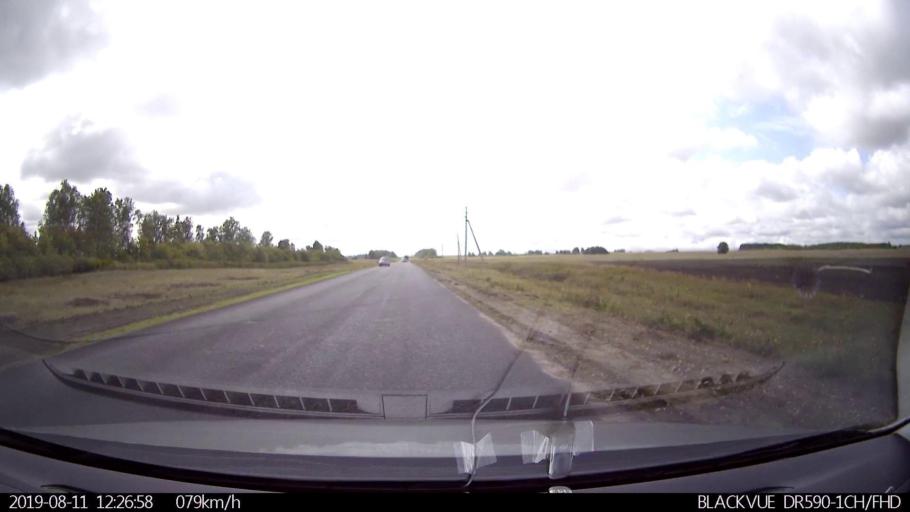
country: RU
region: Ulyanovsk
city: Ignatovka
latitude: 53.8596
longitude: 47.9267
